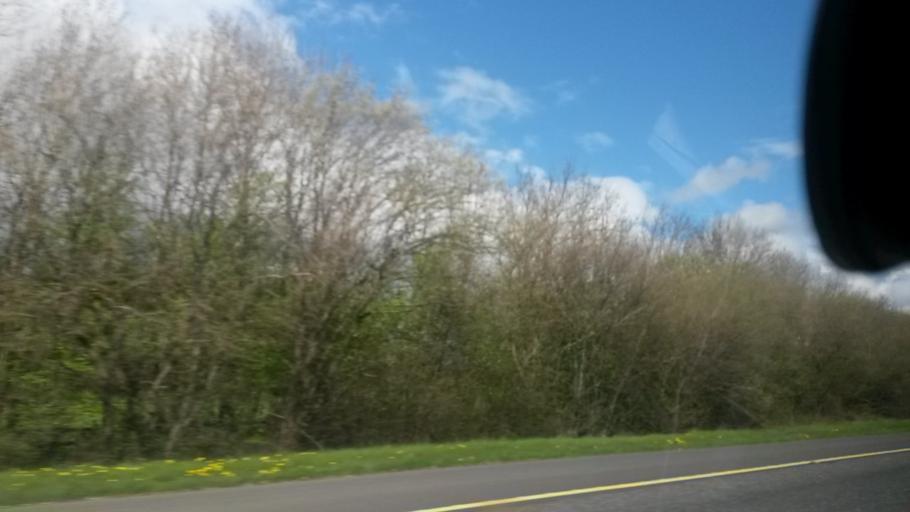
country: IE
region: Leinster
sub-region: Kildare
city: Kilcullen
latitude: 53.1917
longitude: -6.7266
